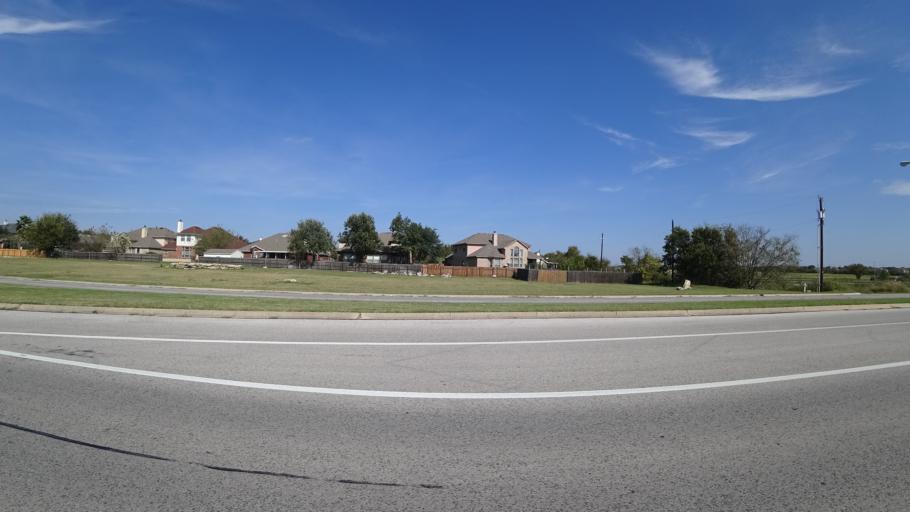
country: US
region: Texas
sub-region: Travis County
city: Pflugerville
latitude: 30.4255
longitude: -97.6281
